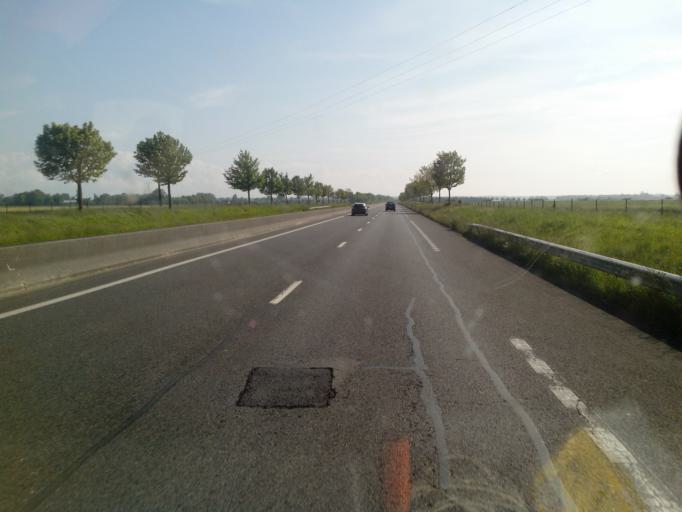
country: FR
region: Picardie
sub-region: Departement de la Somme
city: Bouttencourt
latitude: 49.9836
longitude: 1.6820
